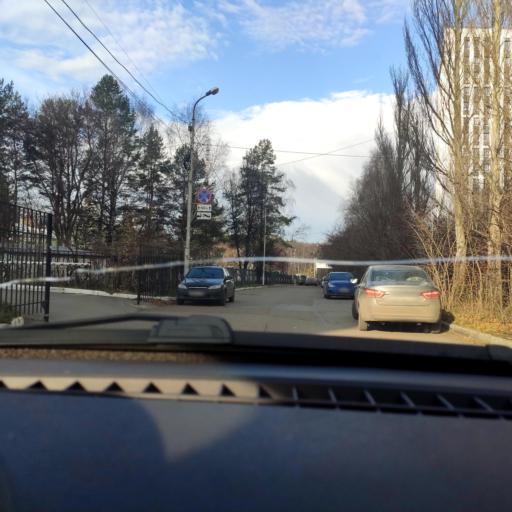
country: RU
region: Bashkortostan
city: Ufa
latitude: 54.7698
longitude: 56.0106
